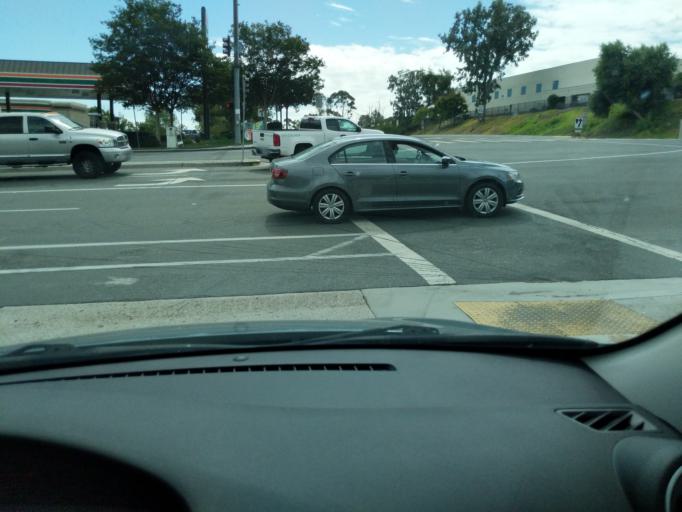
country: US
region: California
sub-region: San Diego County
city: San Diego
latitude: 32.8085
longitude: -117.1222
